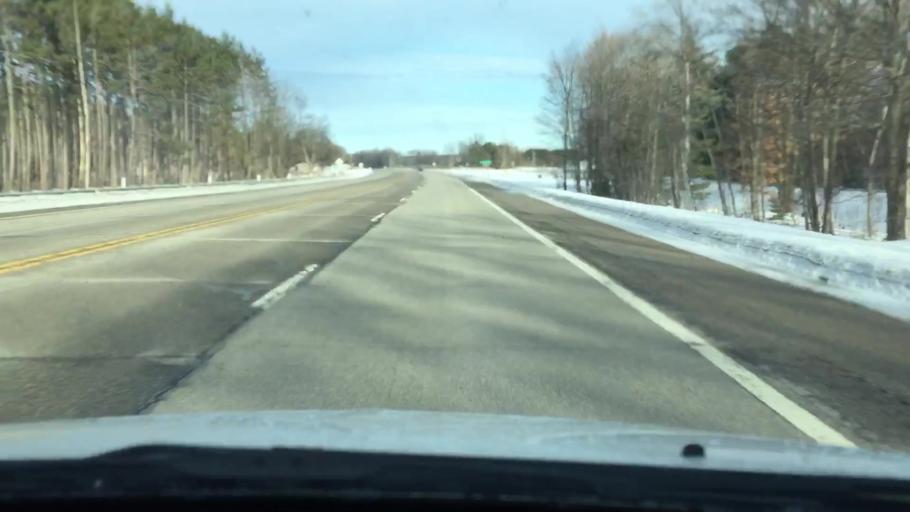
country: US
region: Michigan
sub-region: Kalkaska County
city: Kalkaska
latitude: 44.6094
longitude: -85.3153
